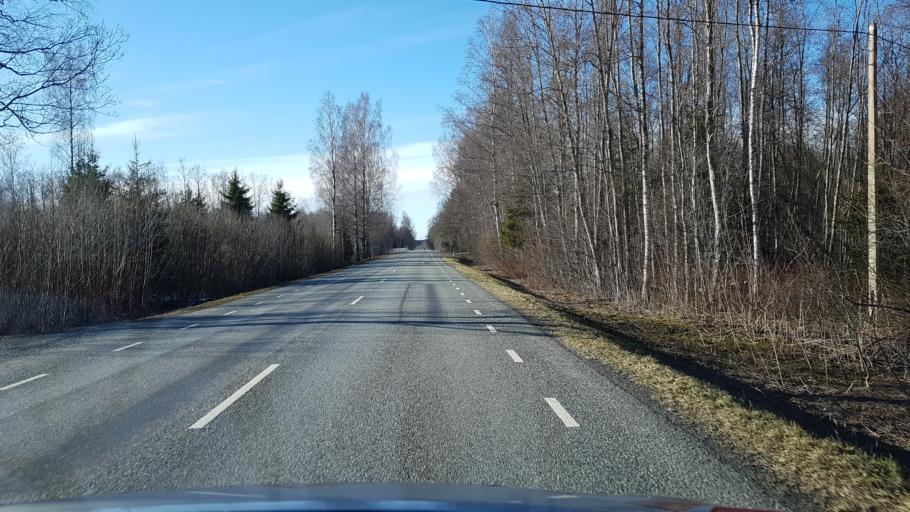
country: EE
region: Laeaene-Virumaa
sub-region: Tapa vald
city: Tapa
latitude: 59.4381
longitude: 25.9601
